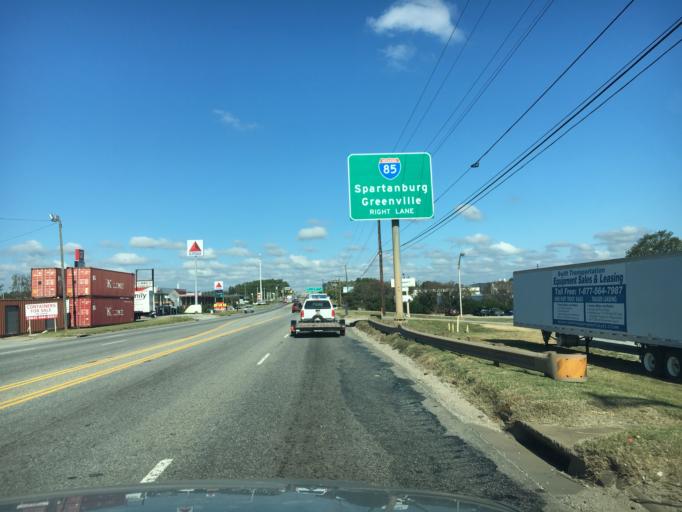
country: US
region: South Carolina
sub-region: Spartanburg County
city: Duncan
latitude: 34.8881
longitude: -82.1551
